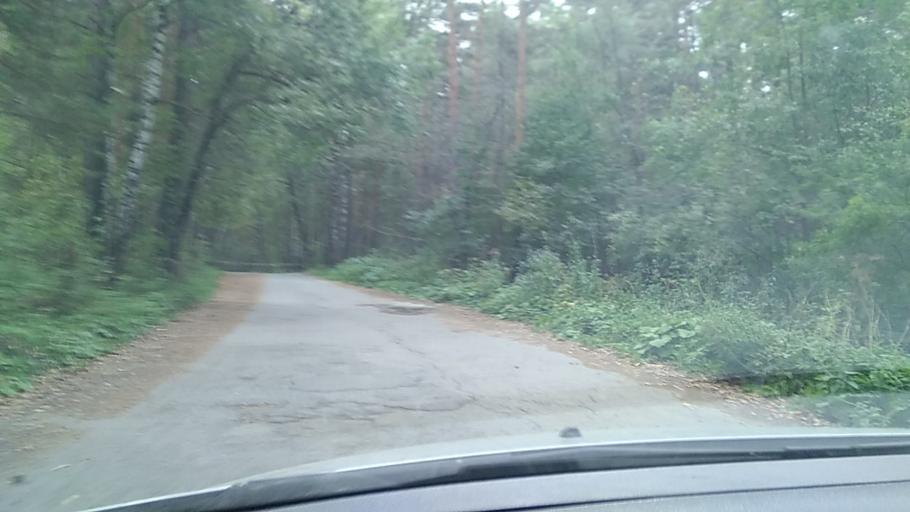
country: RU
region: Chelyabinsk
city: Zlatoust
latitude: 55.1559
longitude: 59.6981
